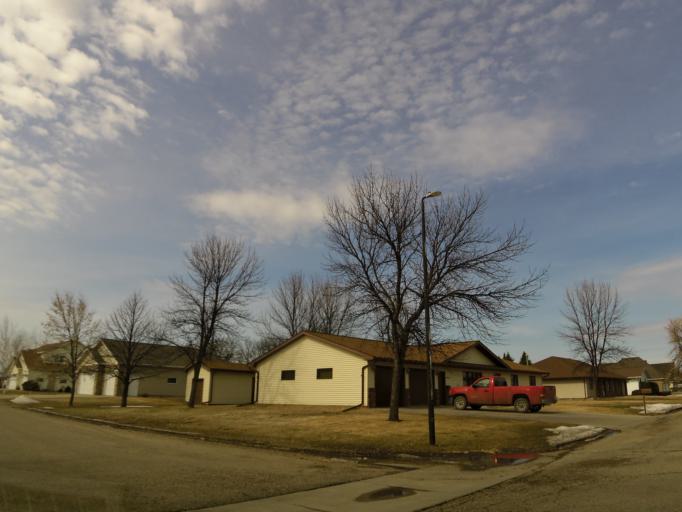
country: US
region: North Dakota
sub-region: Walsh County
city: Grafton
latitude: 48.4047
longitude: -97.4160
